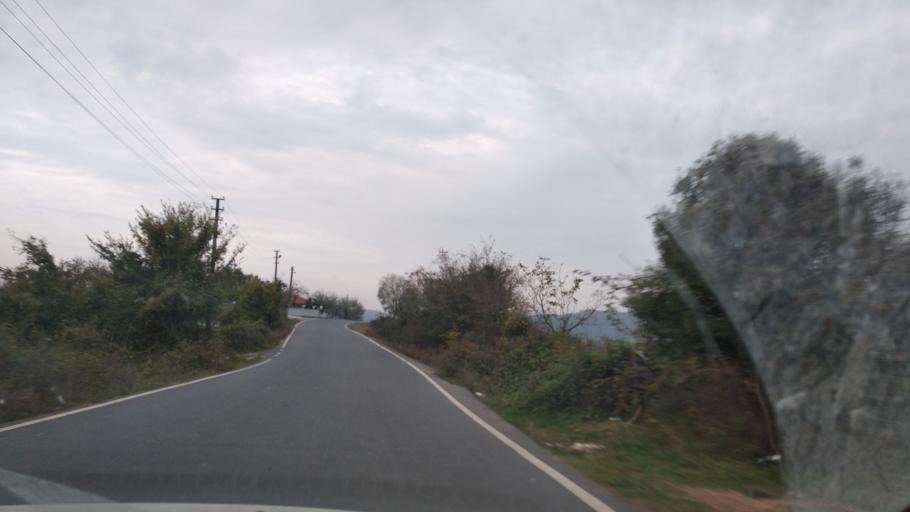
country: TR
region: Sakarya
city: Ortakoy
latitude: 41.0368
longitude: 30.6558
